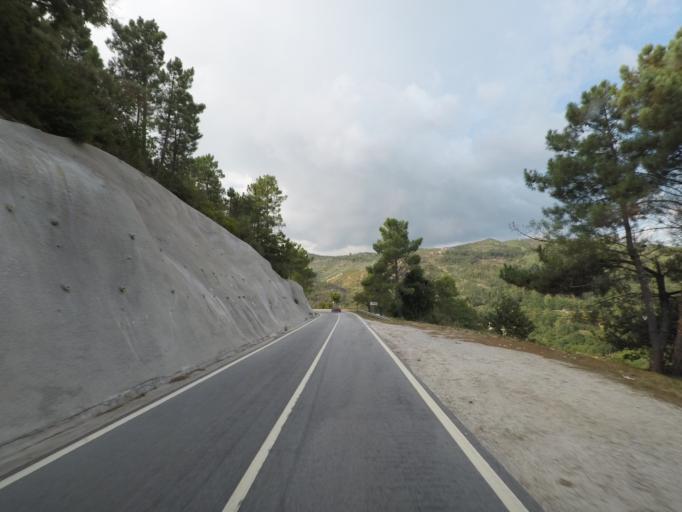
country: PT
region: Porto
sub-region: Baiao
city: Valadares
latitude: 41.2120
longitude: -7.9768
